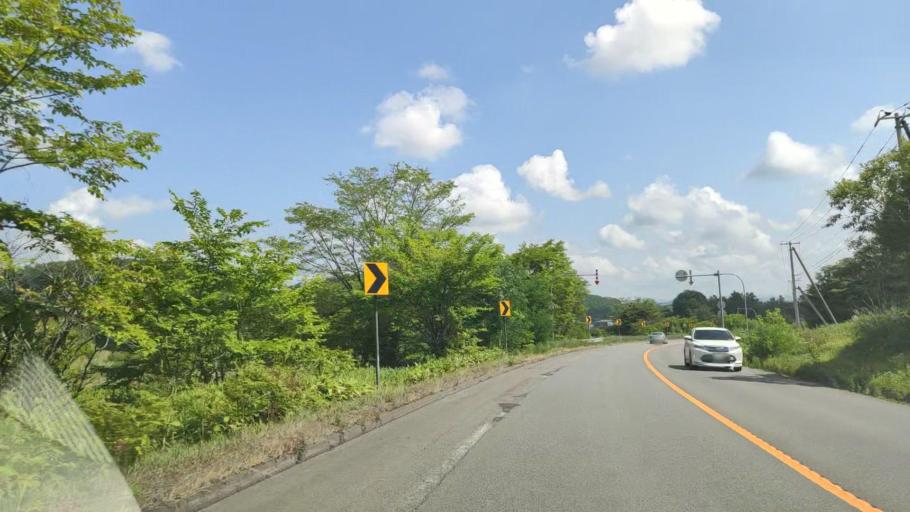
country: JP
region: Hokkaido
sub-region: Asahikawa-shi
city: Asahikawa
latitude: 43.5865
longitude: 142.4448
